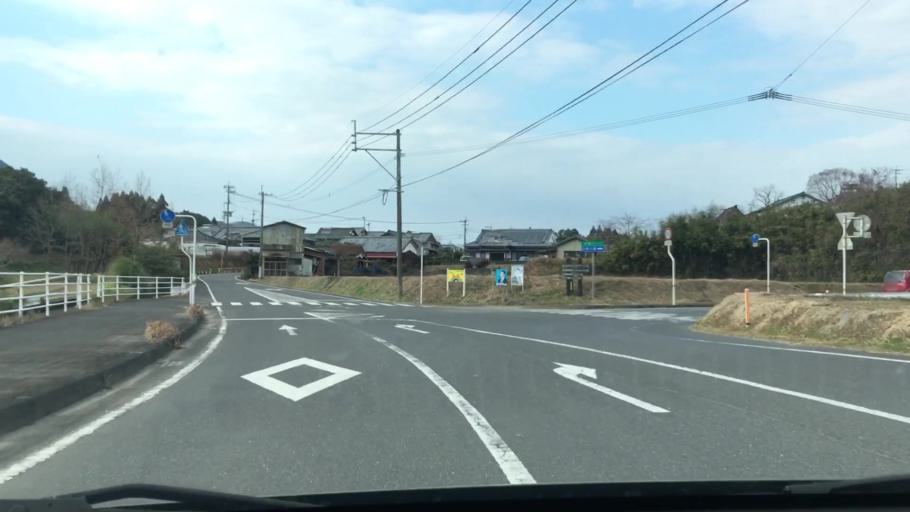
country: JP
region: Miyazaki
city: Kushima
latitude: 31.5006
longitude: 131.2388
